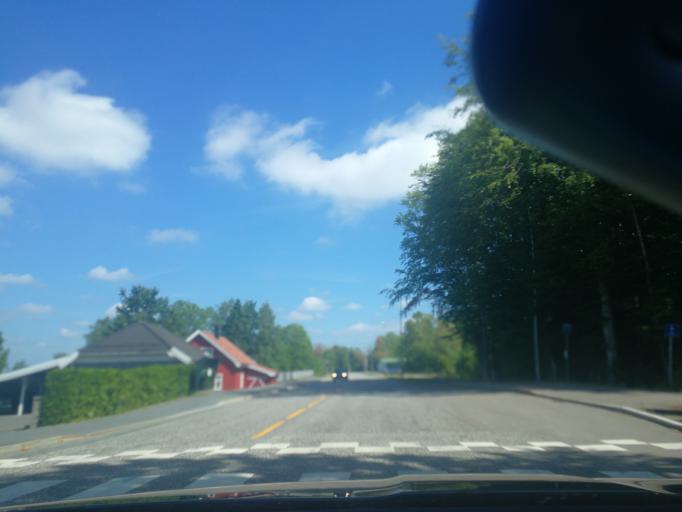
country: NO
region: Vestfold
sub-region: Sandefjord
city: Sandefjord
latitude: 59.1946
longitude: 10.2305
